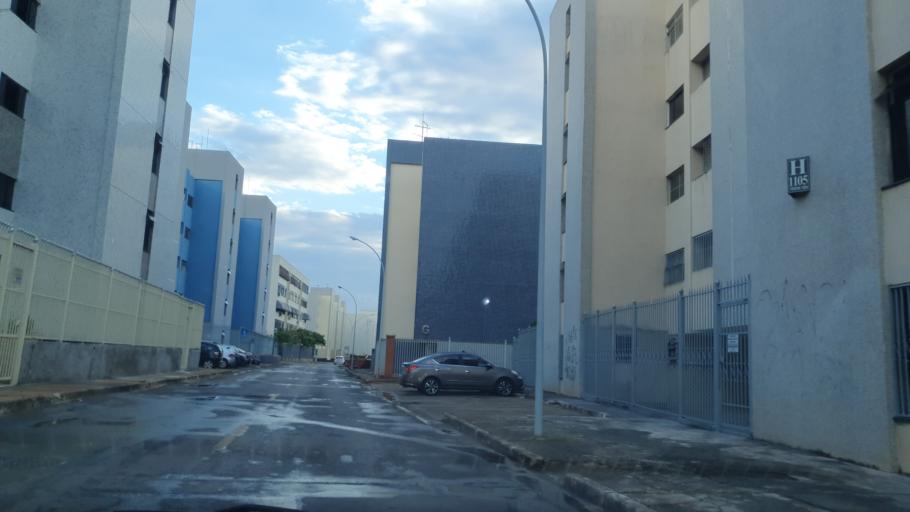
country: BR
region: Federal District
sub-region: Brasilia
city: Brasilia
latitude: -15.7961
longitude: -47.9370
